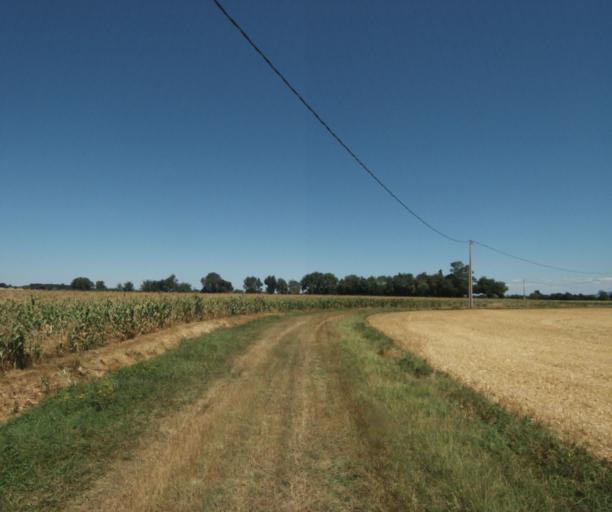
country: FR
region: Midi-Pyrenees
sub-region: Departement de la Haute-Garonne
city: Saint-Felix-Lauragais
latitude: 43.4824
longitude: 1.9420
